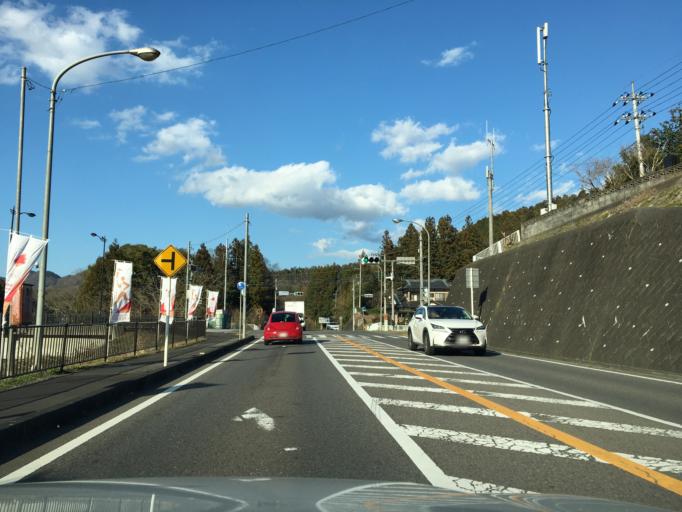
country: JP
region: Ibaraki
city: Daigo
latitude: 36.7437
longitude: 140.3825
